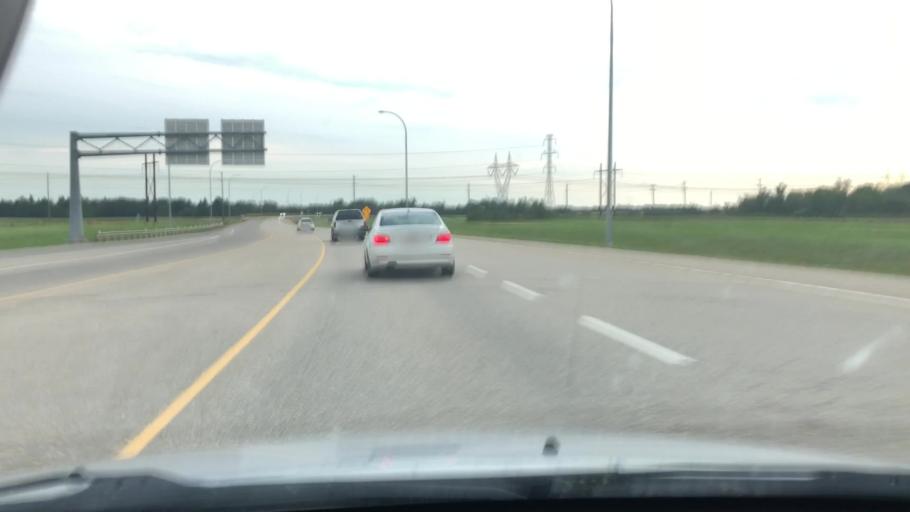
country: CA
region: Alberta
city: Devon
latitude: 53.4640
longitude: -113.6355
